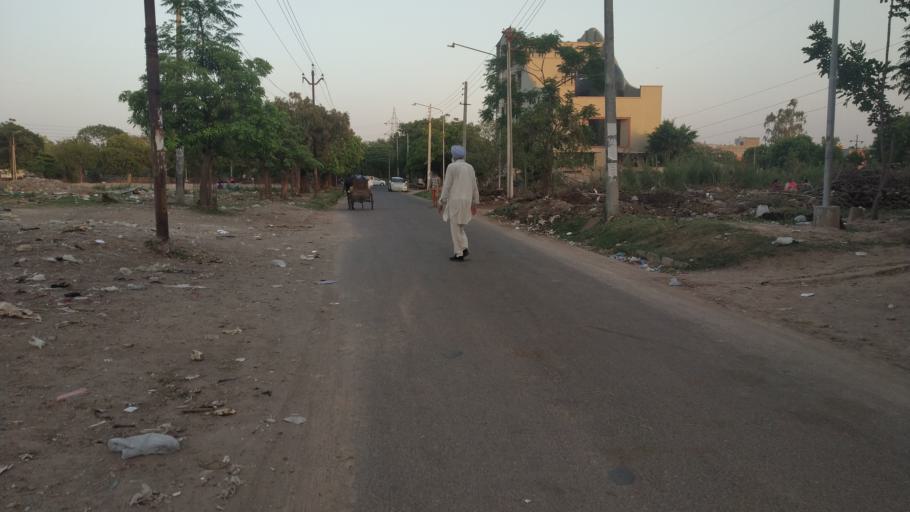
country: IN
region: Punjab
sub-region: Ajitgarh
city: Mohali
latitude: 30.6899
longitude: 76.7284
